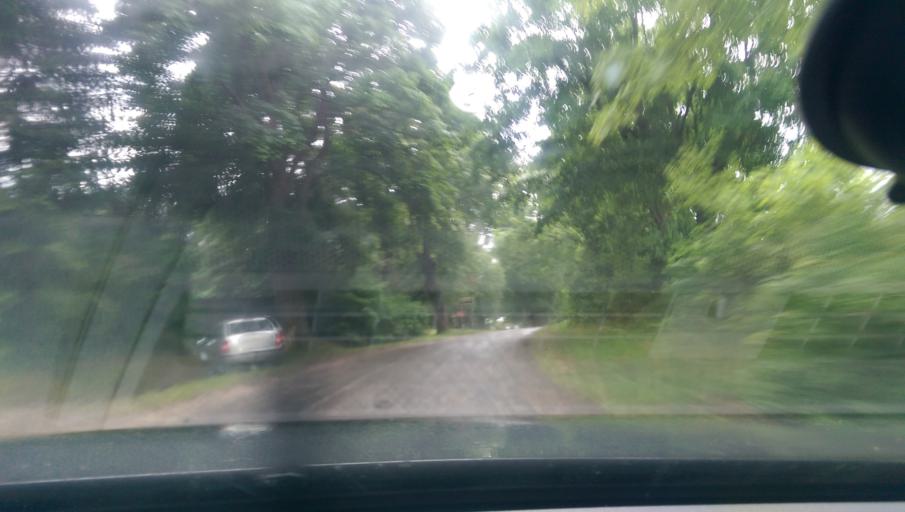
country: PL
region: Warmian-Masurian Voivodeship
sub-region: Powiat mragowski
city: Piecki
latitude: 53.8264
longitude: 21.3903
